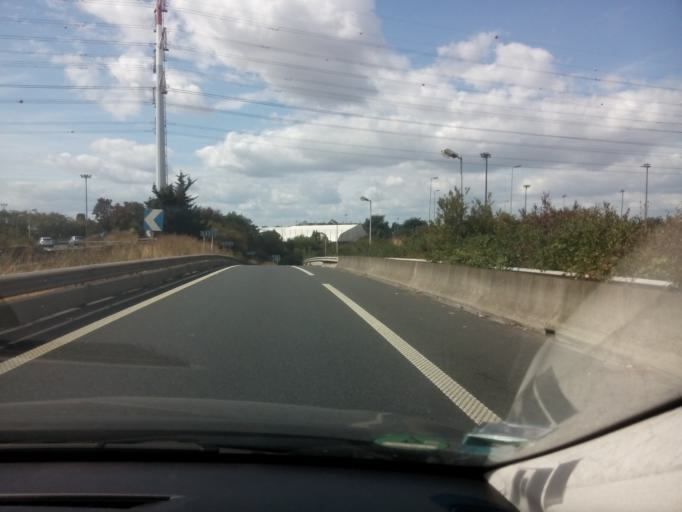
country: FR
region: Ile-de-France
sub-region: Departement du Val-de-Marne
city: Chevilly-Larue
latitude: 48.7583
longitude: 2.3392
